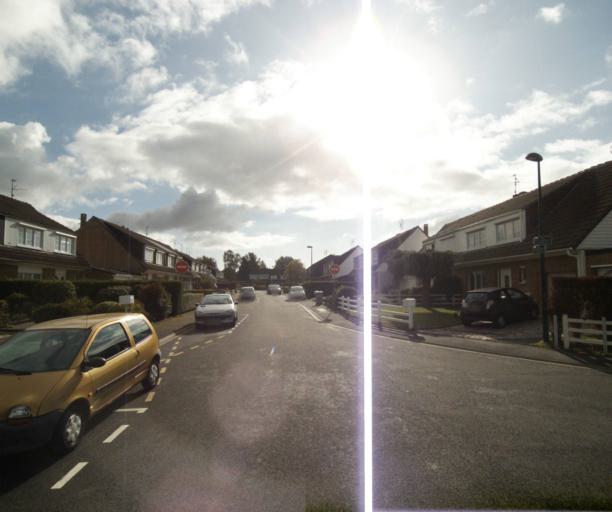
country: FR
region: Nord-Pas-de-Calais
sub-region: Departement du Nord
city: Verlinghem
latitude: 50.6848
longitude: 2.9977
